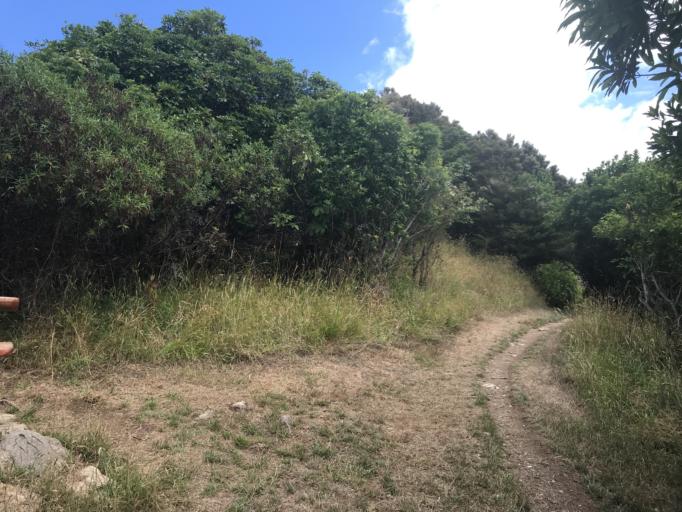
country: NZ
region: Marlborough
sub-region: Marlborough District
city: Picton
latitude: -41.2147
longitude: 173.9882
